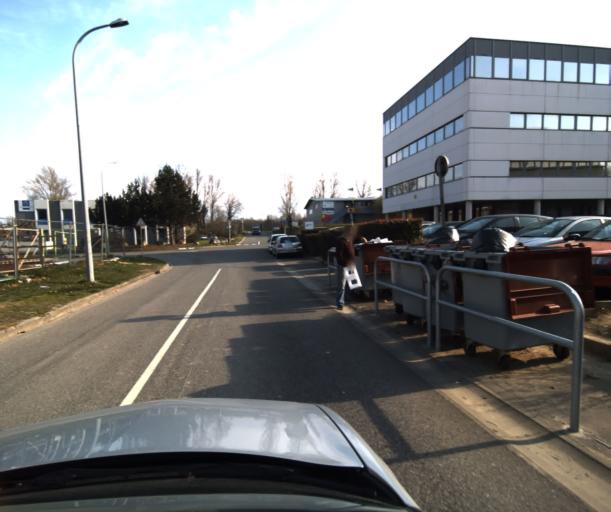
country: FR
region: Midi-Pyrenees
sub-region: Departement de la Haute-Garonne
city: Ramonville-Saint-Agne
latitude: 43.5498
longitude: 1.4854
